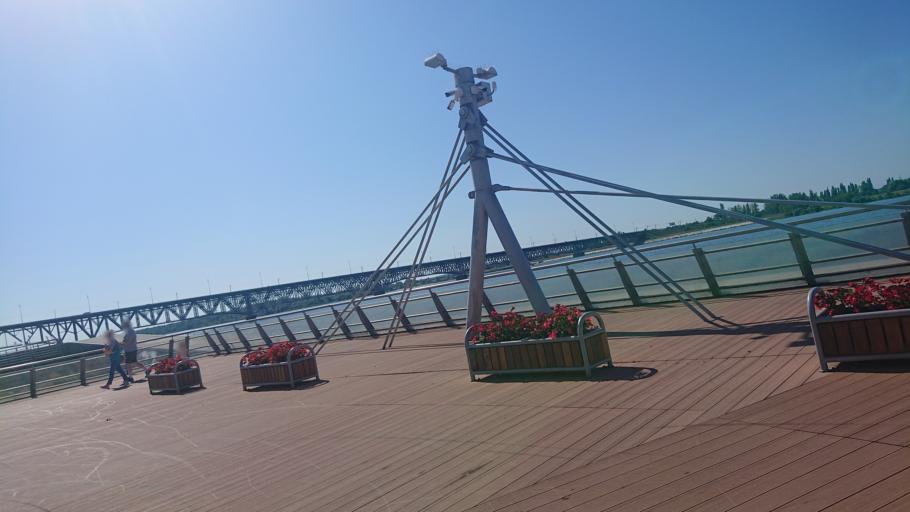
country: PL
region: Masovian Voivodeship
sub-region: Plock
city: Plock
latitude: 52.5392
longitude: 19.6887
